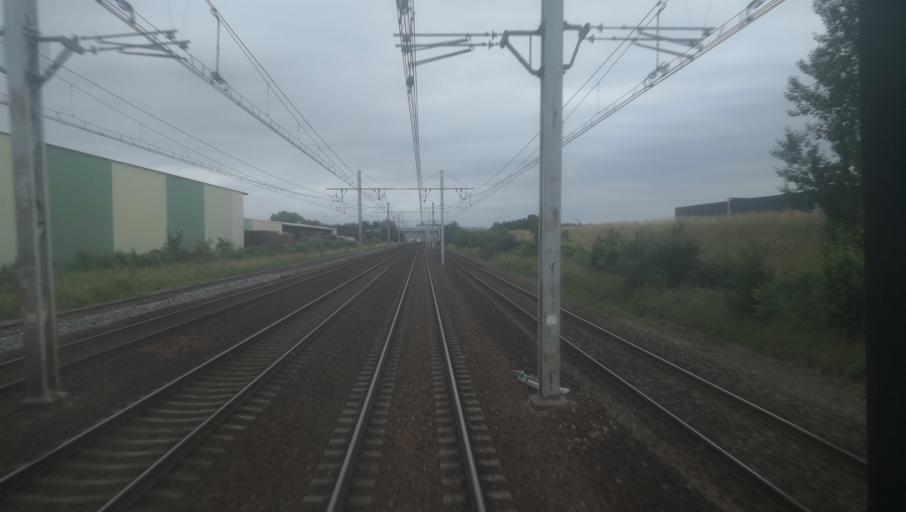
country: FR
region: Ile-de-France
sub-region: Departement de l'Essonne
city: Marolles-en-Hurepoix
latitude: 48.5726
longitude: 2.2902
